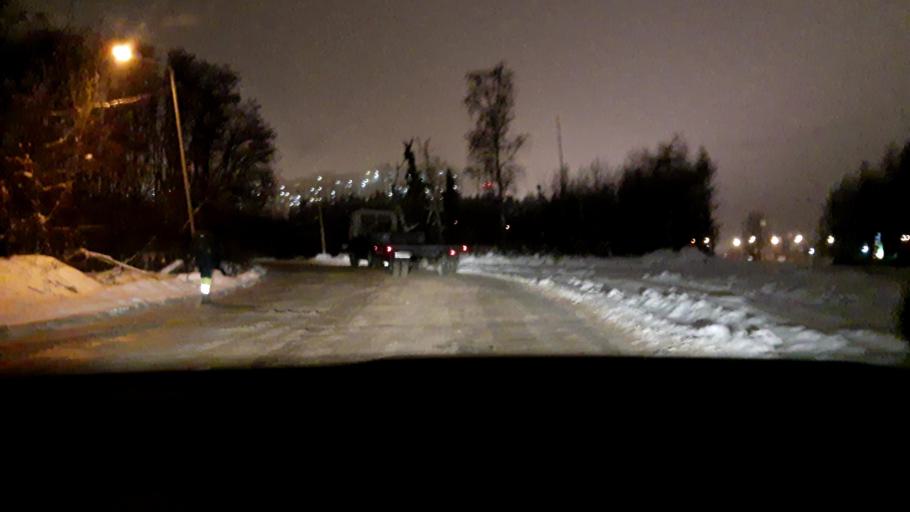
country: RU
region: Moscow
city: Annino
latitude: 55.5537
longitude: 37.5902
